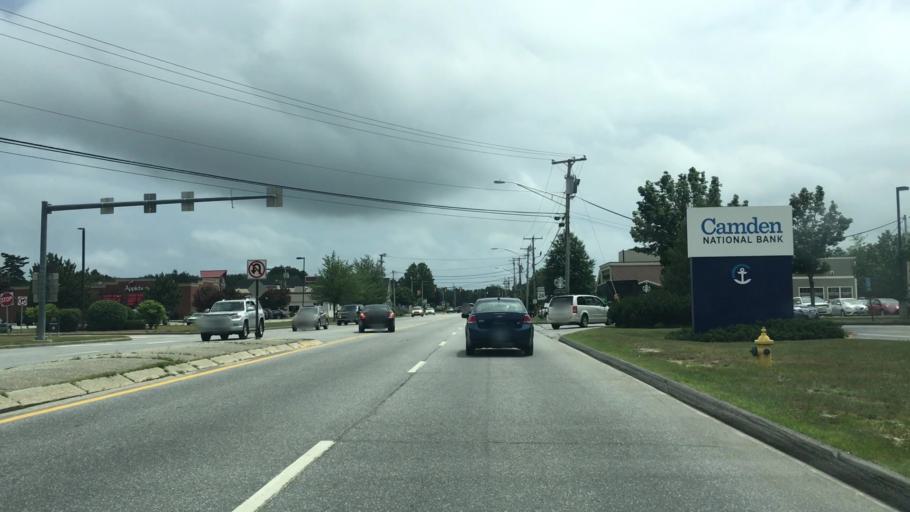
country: US
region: Maine
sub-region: Cumberland County
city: Brunswick
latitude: 43.9071
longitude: -69.9161
